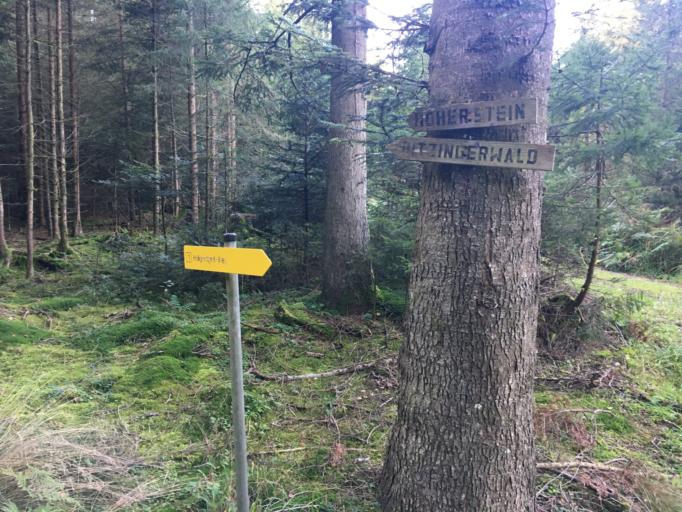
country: AT
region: Upper Austria
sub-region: Politischer Bezirk Vocklabruck
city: Frankenmarkt
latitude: 48.0031
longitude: 13.3958
